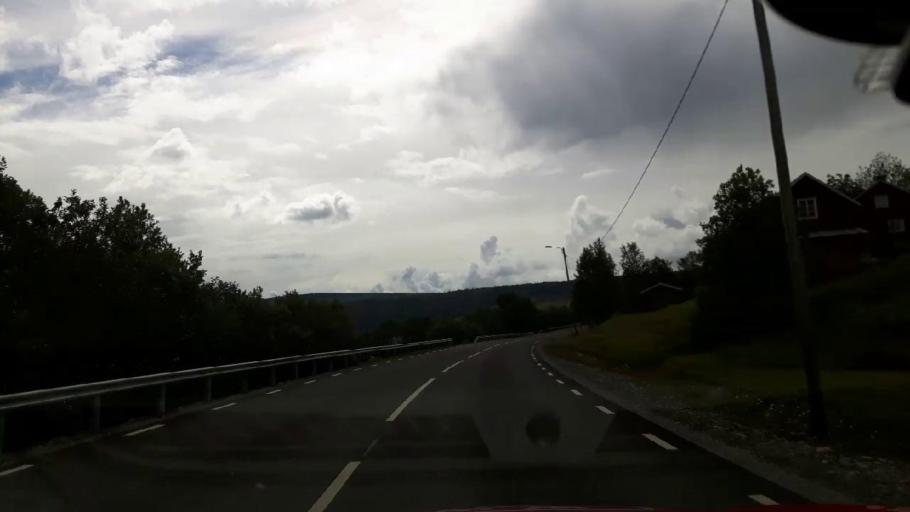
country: NO
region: Nord-Trondelag
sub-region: Royrvik
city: Royrvik
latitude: 64.8037
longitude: 14.0712
